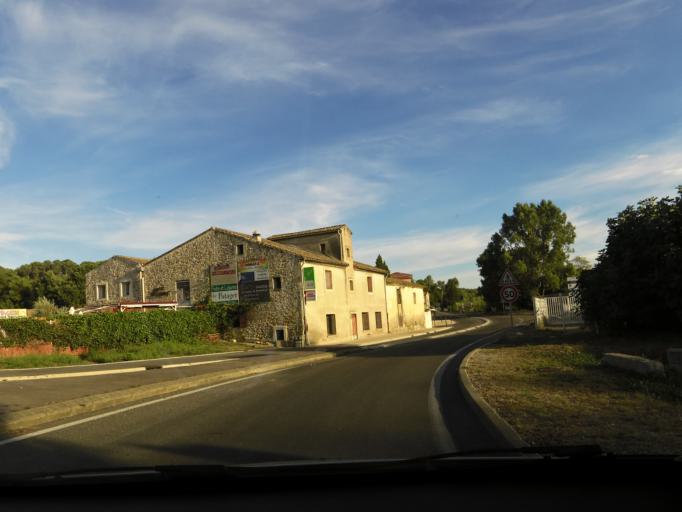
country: FR
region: Languedoc-Roussillon
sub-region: Departement de l'Herault
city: Montferrier-sur-Lez
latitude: 43.6762
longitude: 3.8670
